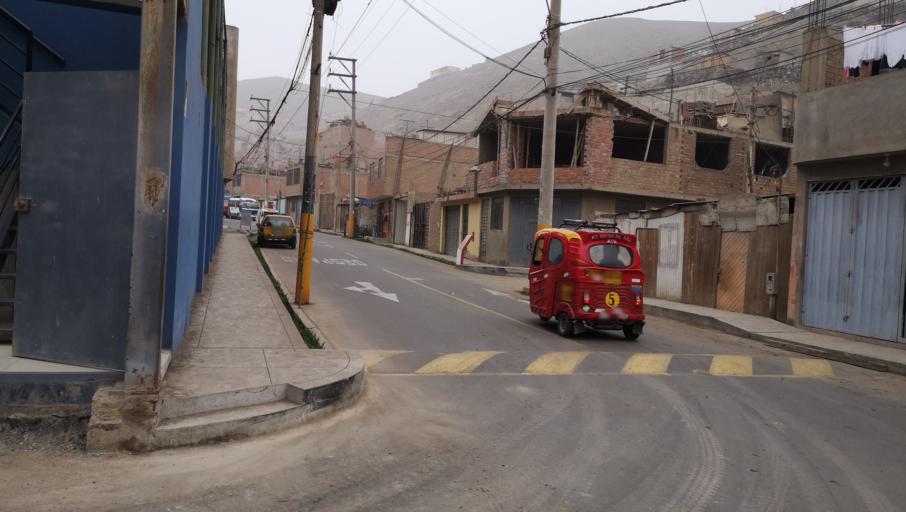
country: PE
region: Lima
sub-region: Lima
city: Vitarte
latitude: -12.0332
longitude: -76.9148
